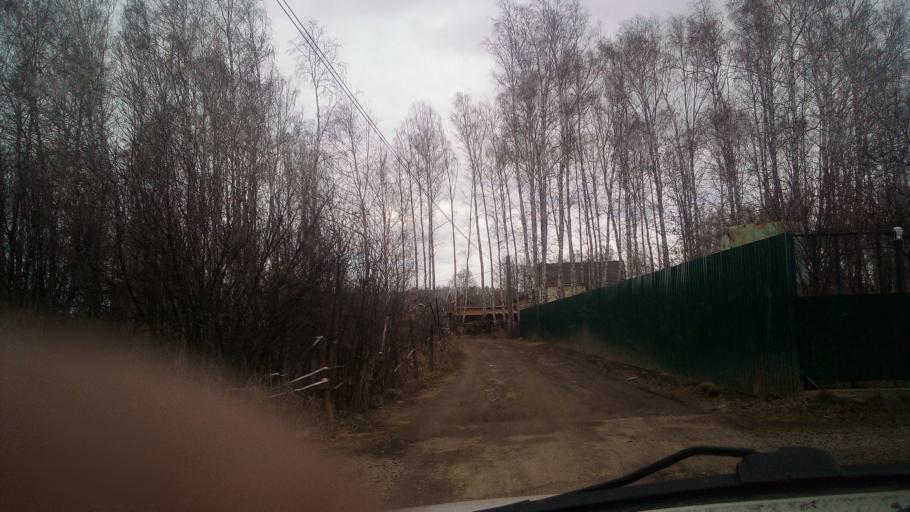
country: RU
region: Chelyabinsk
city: Sargazy
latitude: 55.1275
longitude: 61.2458
